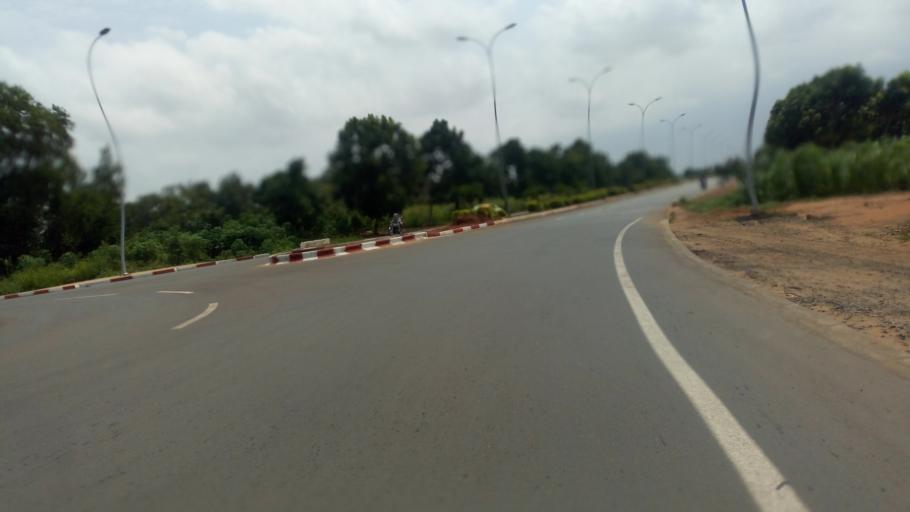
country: TG
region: Maritime
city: Lome
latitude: 6.1929
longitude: 1.2271
